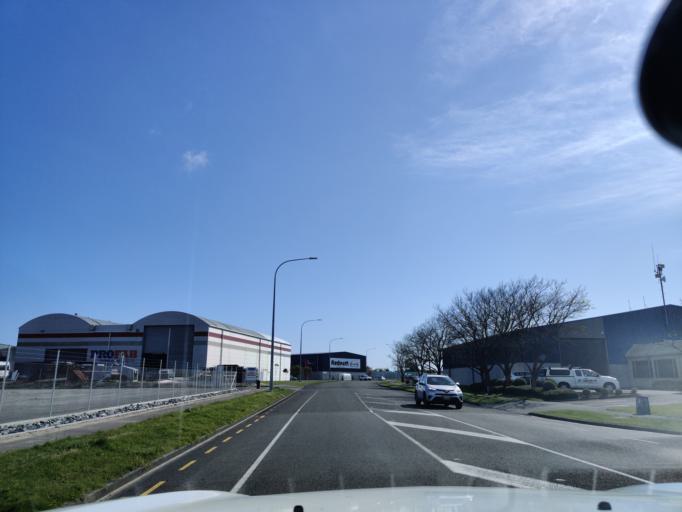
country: NZ
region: Manawatu-Wanganui
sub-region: Palmerston North City
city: Palmerston North
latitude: -40.3358
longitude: 175.6444
